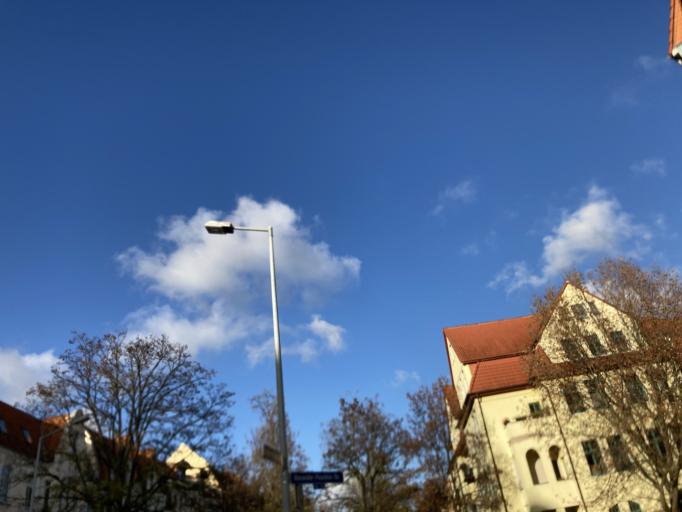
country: DE
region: Saxony-Anhalt
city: Magdeburg
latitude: 52.1321
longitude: 11.6163
